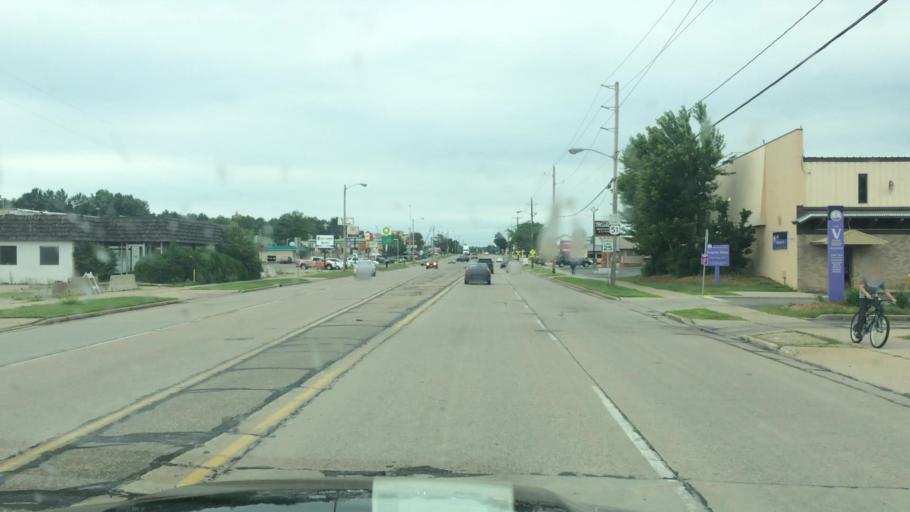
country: US
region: Wisconsin
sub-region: Portage County
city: Stevens Point
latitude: 44.5294
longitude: -89.5748
